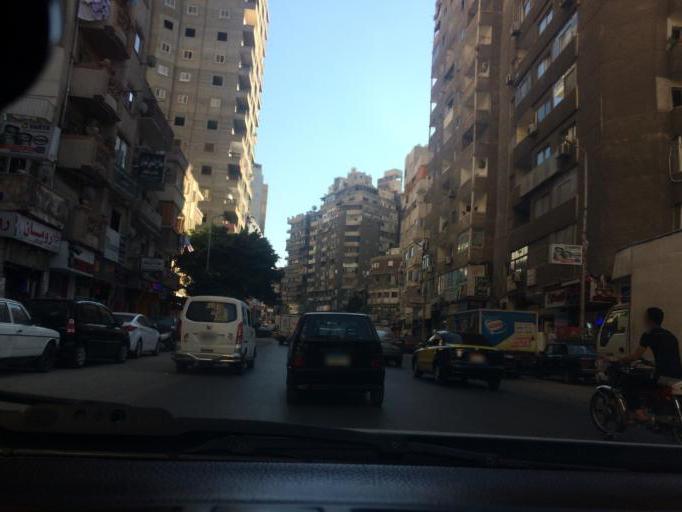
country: EG
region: Alexandria
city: Alexandria
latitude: 31.2505
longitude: 29.9817
